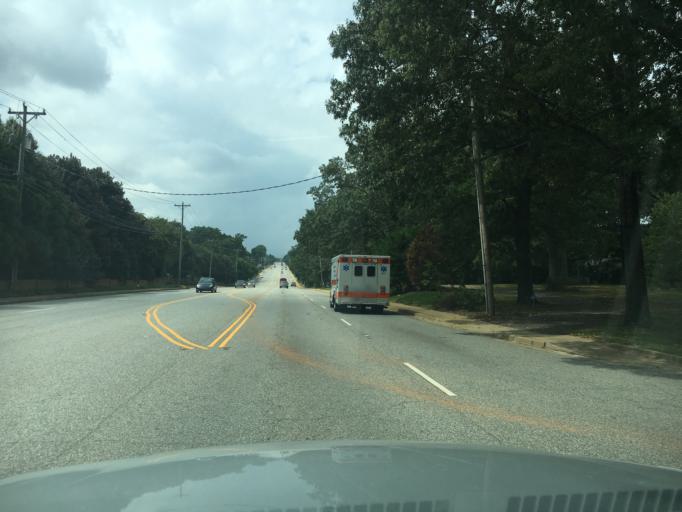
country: US
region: South Carolina
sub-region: Greenville County
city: Wade Hampton
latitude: 34.8565
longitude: -82.3085
